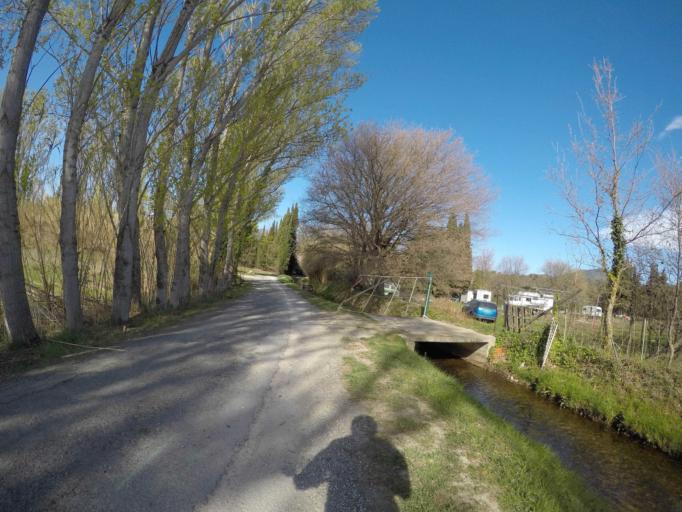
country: FR
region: Languedoc-Roussillon
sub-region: Departement des Pyrenees-Orientales
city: Corneilla-la-Riviere
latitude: 42.6987
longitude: 2.7133
